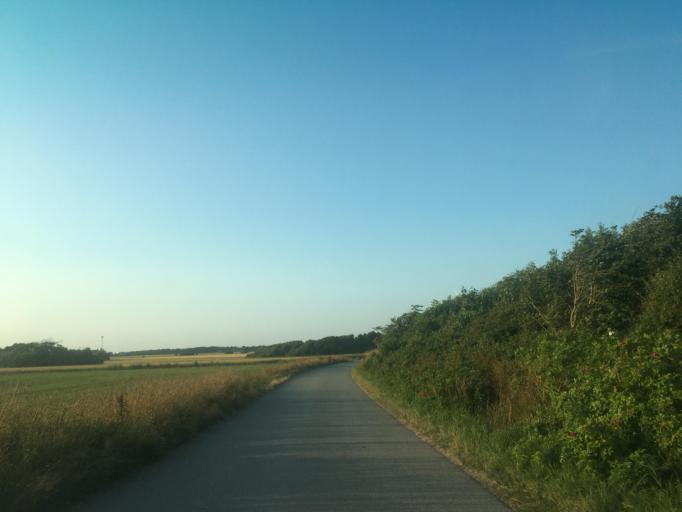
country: DK
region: North Denmark
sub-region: Thisted Kommune
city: Hurup
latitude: 56.8199
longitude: 8.3388
